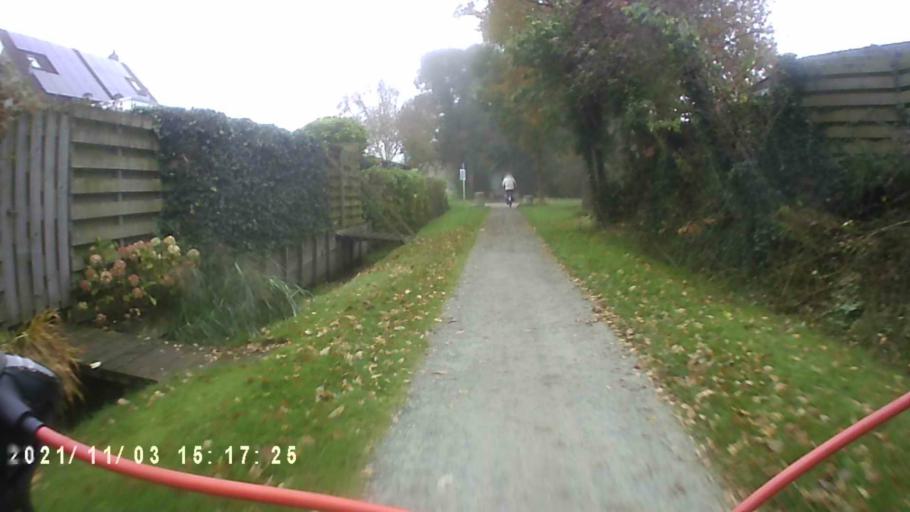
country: NL
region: Groningen
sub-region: Gemeente Leek
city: Leek
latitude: 53.1636
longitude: 6.3623
